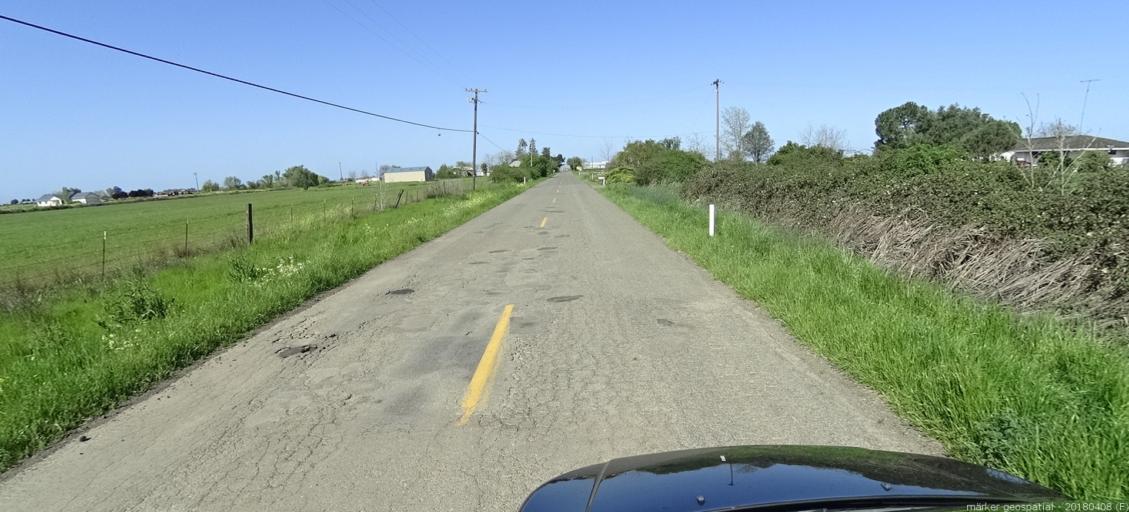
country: US
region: California
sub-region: Sacramento County
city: Laguna
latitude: 38.3503
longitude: -121.4296
